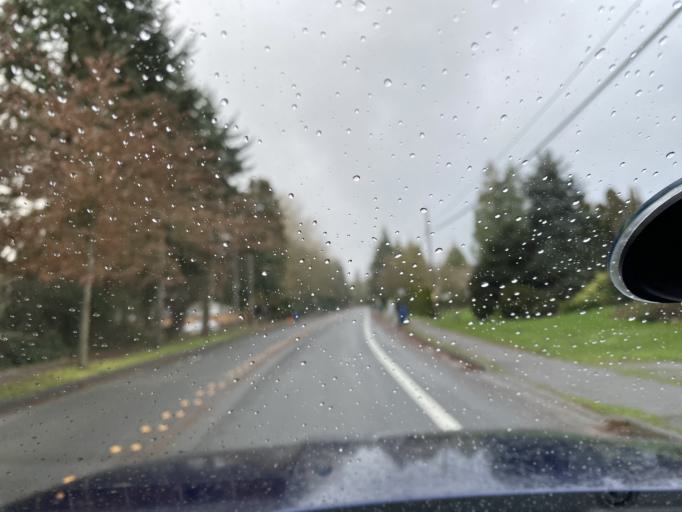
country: US
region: Washington
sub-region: King County
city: Redmond
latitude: 47.6563
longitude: -122.1242
